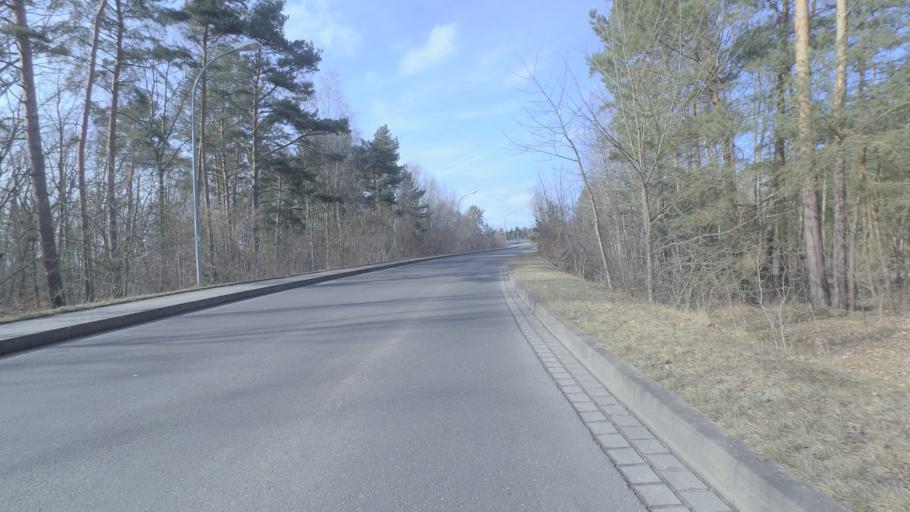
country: DE
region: Brandenburg
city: Ludwigsfelde
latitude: 52.3048
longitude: 13.2717
